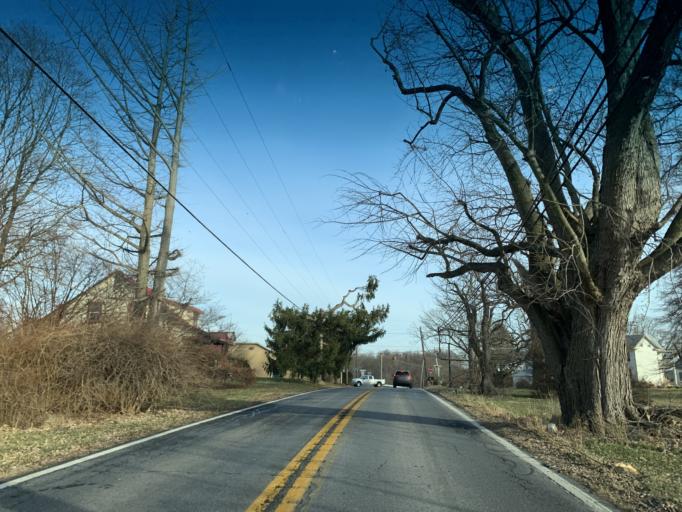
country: US
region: Maryland
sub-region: Carroll County
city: Hampstead
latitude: 39.6018
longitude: -76.7751
